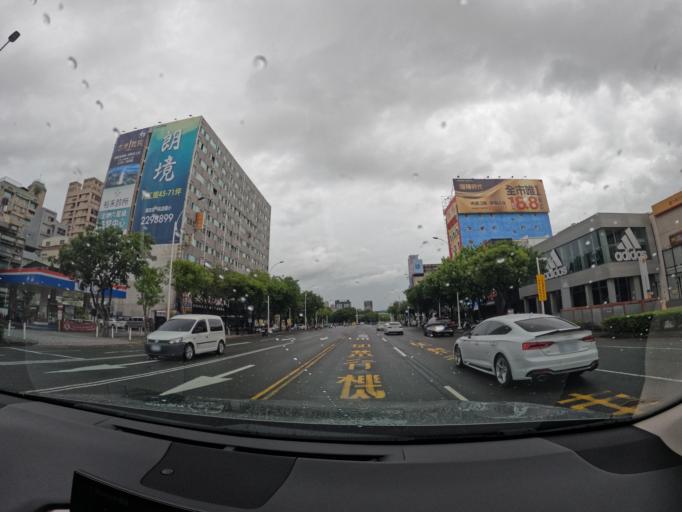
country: TW
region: Kaohsiung
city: Kaohsiung
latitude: 22.6213
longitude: 120.3018
